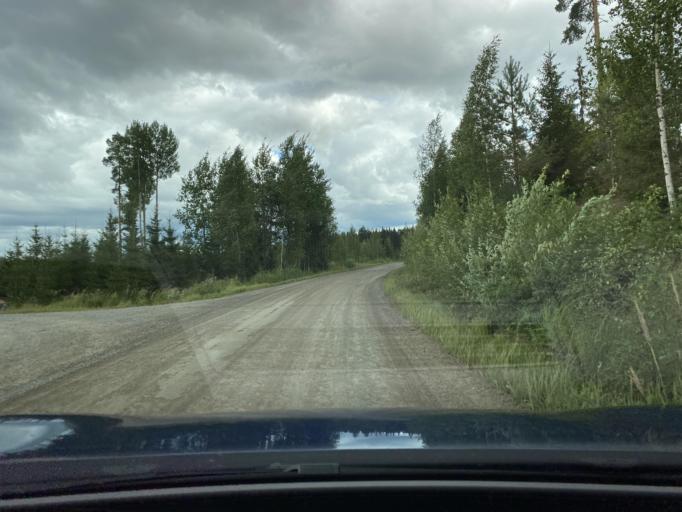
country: FI
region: Pirkanmaa
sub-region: Lounais-Pirkanmaa
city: Punkalaidun
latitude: 61.2205
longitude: 23.1635
